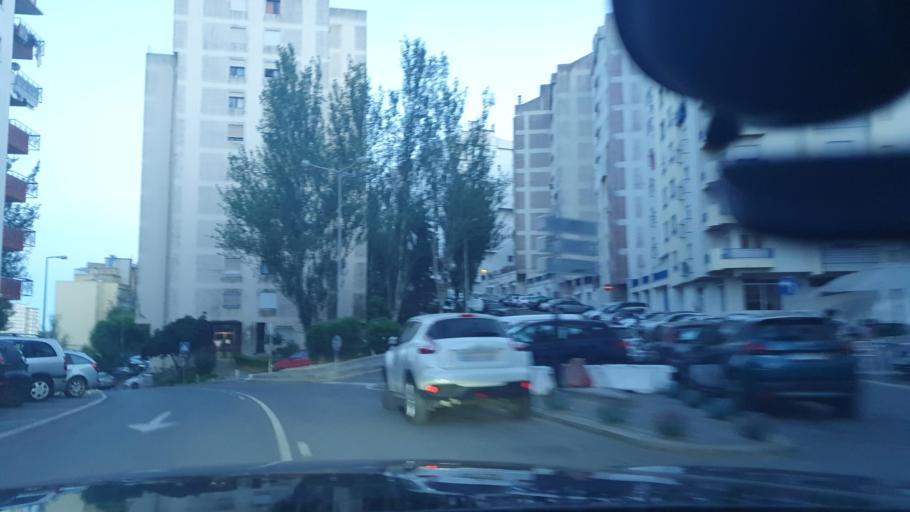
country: PT
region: Lisbon
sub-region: Sintra
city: Queluz
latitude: 38.7645
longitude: -9.2598
